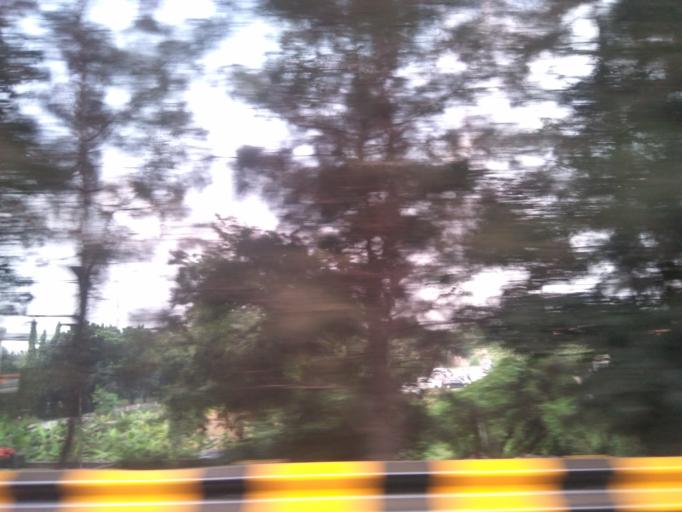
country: ID
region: West Java
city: Bekasi
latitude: -6.2543
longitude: 106.9910
